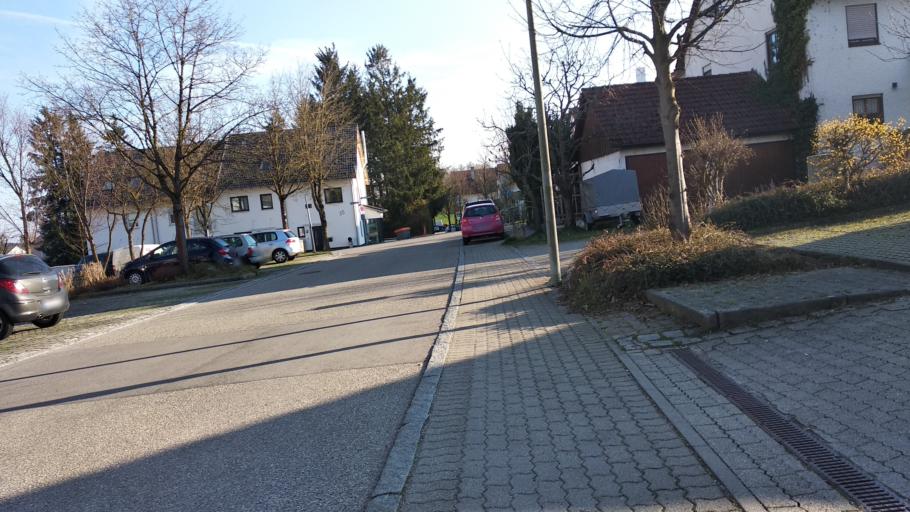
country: DE
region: Bavaria
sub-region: Upper Bavaria
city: Markt Schwaben
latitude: 48.1866
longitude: 11.8653
